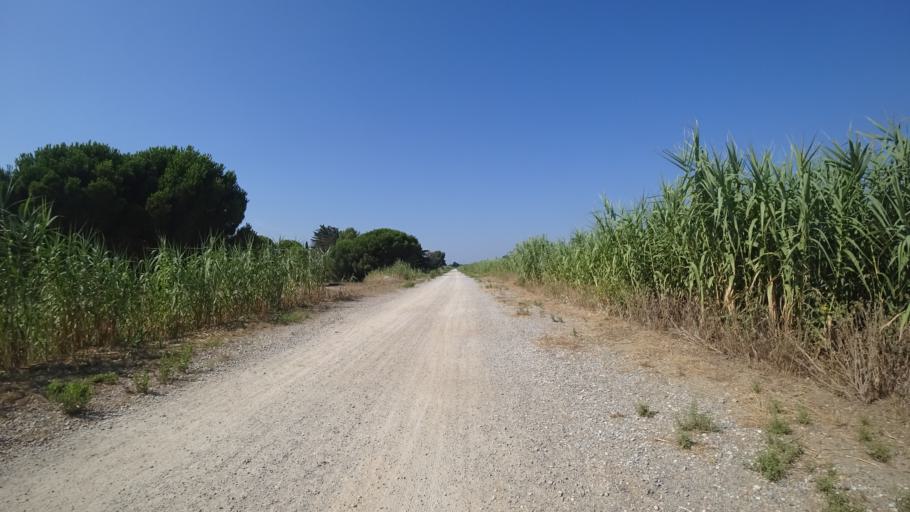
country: FR
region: Languedoc-Roussillon
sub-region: Departement des Pyrenees-Orientales
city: Le Barcares
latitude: 42.7763
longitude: 3.0323
